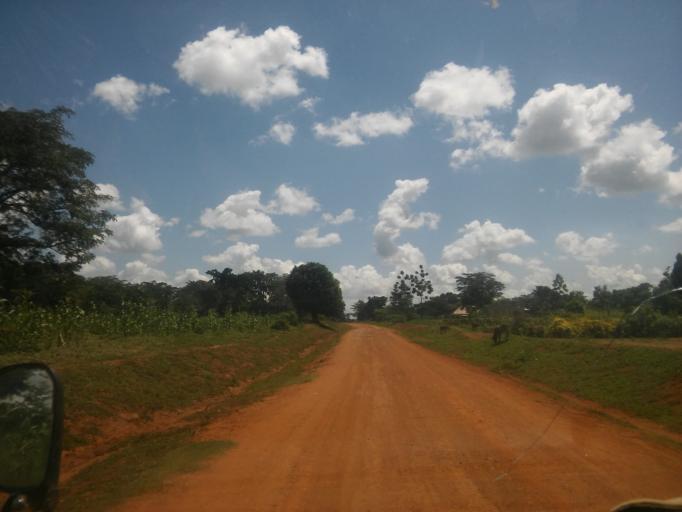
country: UG
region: Eastern Region
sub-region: Budaka District
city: Budaka
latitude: 1.1136
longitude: 33.9502
